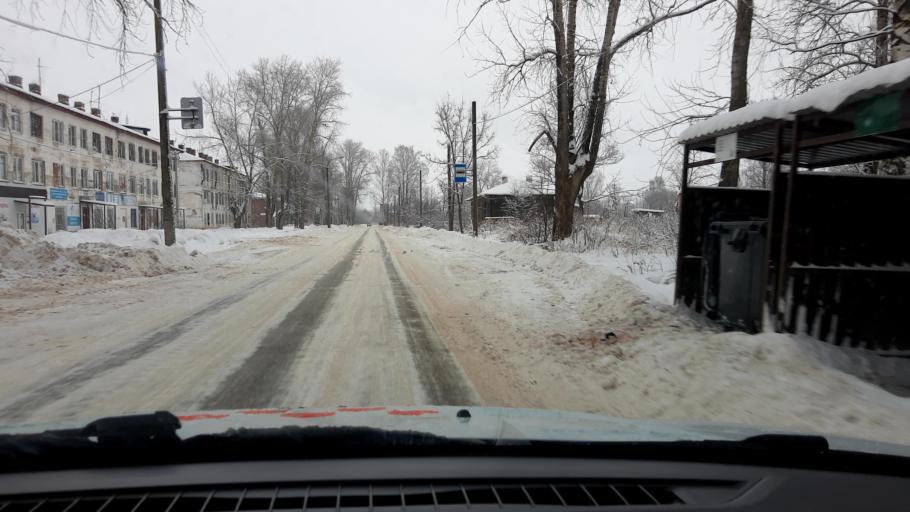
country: RU
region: Nizjnij Novgorod
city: Chkalovsk
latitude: 56.7673
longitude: 43.2560
